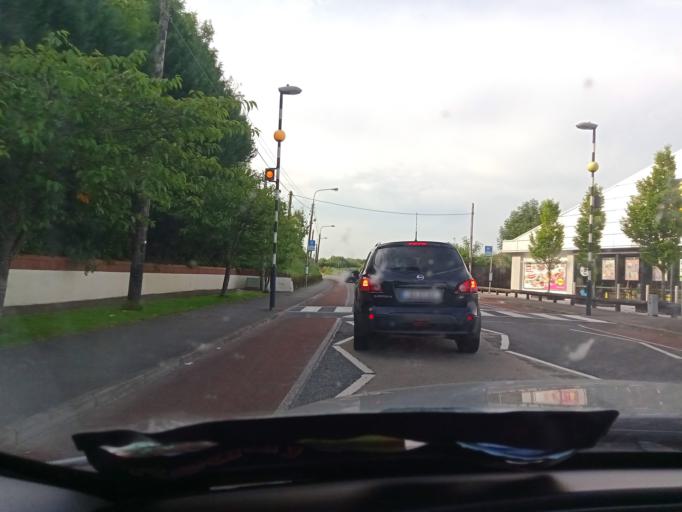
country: IE
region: Ulster
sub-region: An Cabhan
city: Cavan
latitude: 53.9764
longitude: -7.3544
